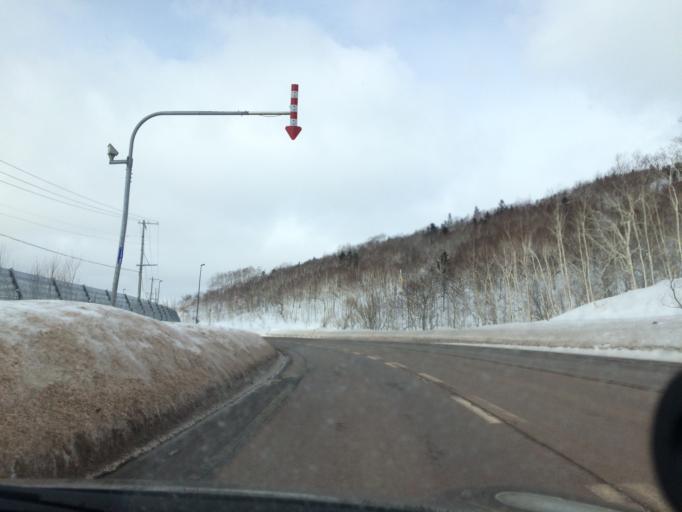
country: JP
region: Hokkaido
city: Shimo-furano
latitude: 43.1298
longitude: 142.7630
